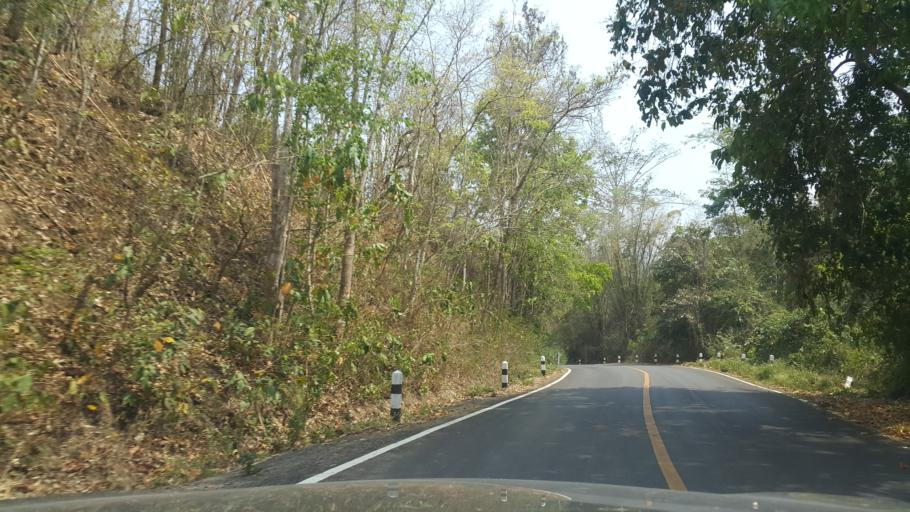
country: TH
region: Lamphun
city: Thung Hua Chang
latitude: 17.9022
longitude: 99.1297
